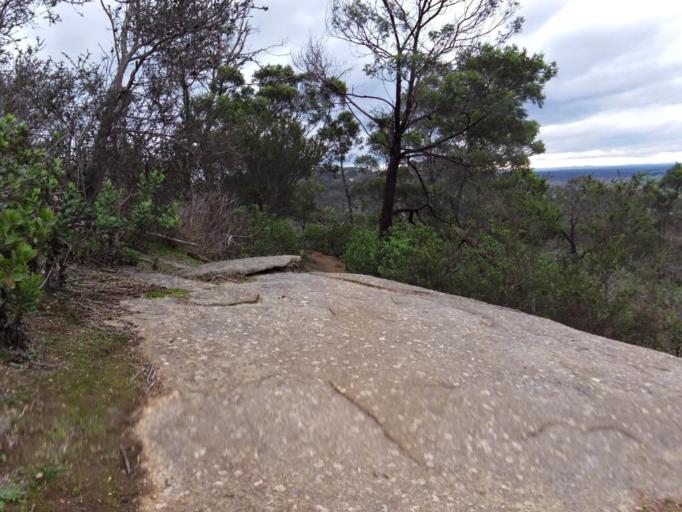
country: AU
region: Victoria
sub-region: Wyndham
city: Little River
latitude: -37.9317
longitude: 144.4336
